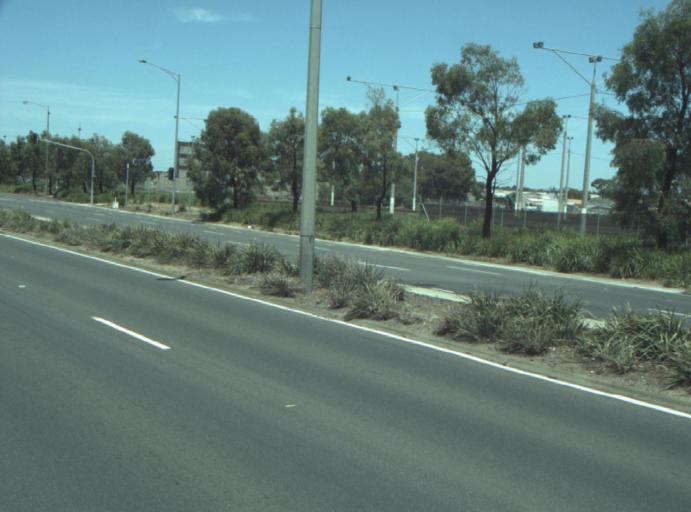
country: AU
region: Victoria
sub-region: Greater Geelong
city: Bell Park
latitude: -38.1187
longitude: 144.3539
